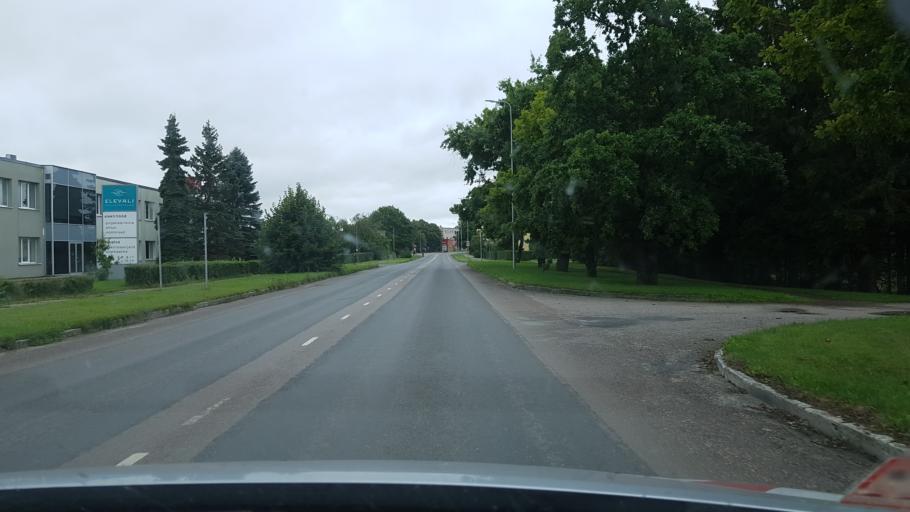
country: EE
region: Viljandimaa
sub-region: Viljandi linn
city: Viljandi
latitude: 58.3767
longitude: 25.5973
